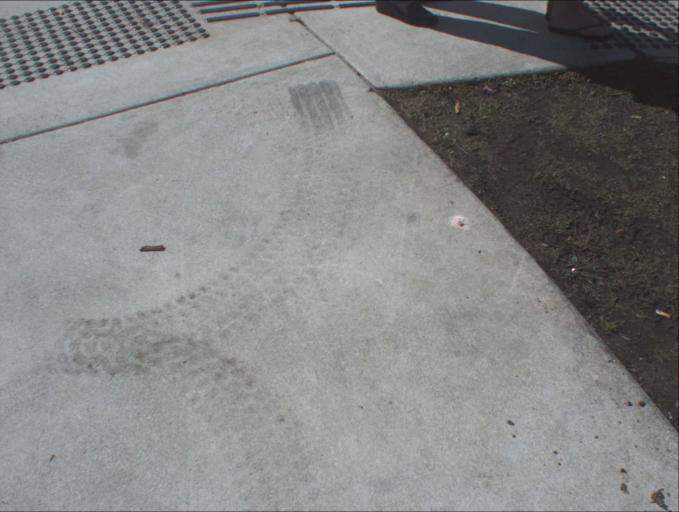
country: AU
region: Queensland
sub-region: Logan
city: Chambers Flat
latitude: -27.8019
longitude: 153.1033
